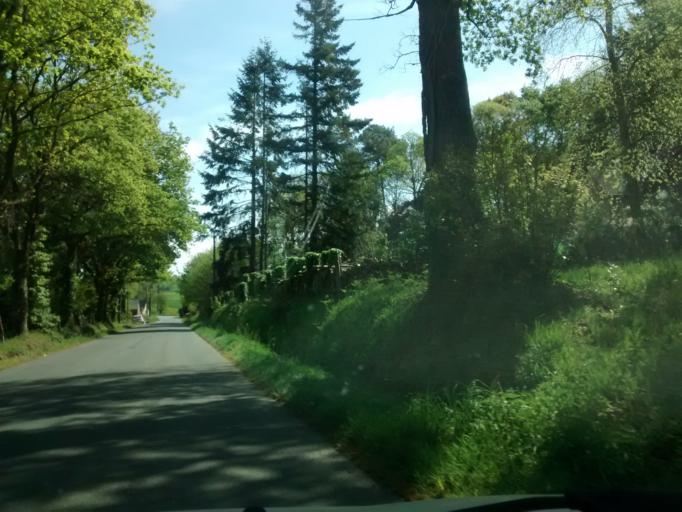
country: FR
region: Brittany
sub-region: Departement d'Ille-et-Vilaine
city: Bain-de-Bretagne
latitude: 47.8232
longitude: -1.7177
